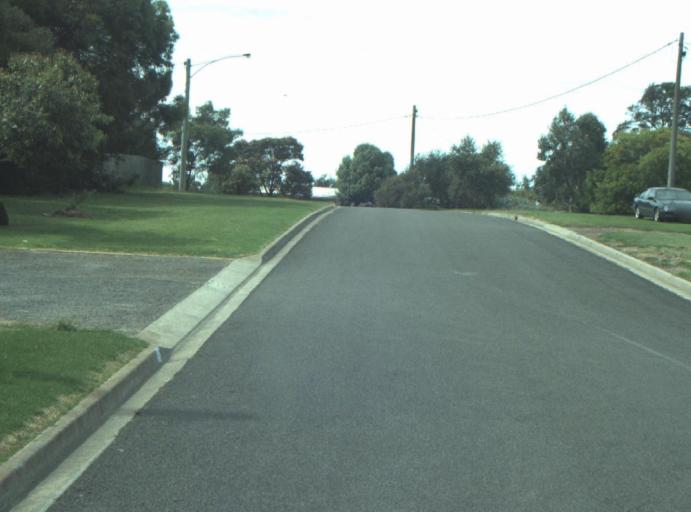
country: AU
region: Victoria
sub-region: Greater Geelong
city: Clifton Springs
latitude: -38.1762
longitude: 144.5631
